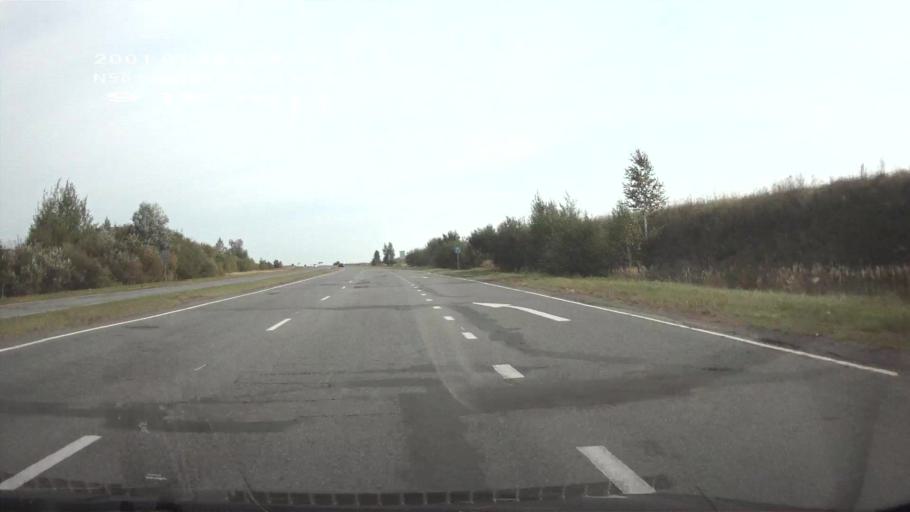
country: RU
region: Mariy-El
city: Yoshkar-Ola
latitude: 56.6895
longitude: 48.0485
